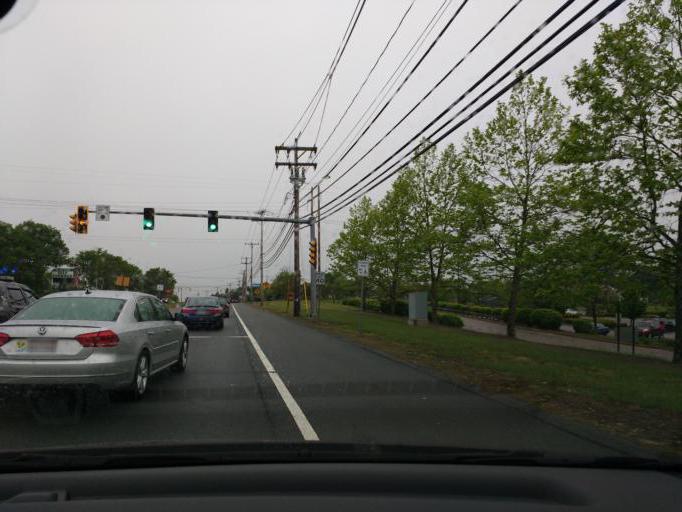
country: US
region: Massachusetts
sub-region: Bristol County
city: Smith Mills
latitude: 41.6408
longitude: -71.0035
